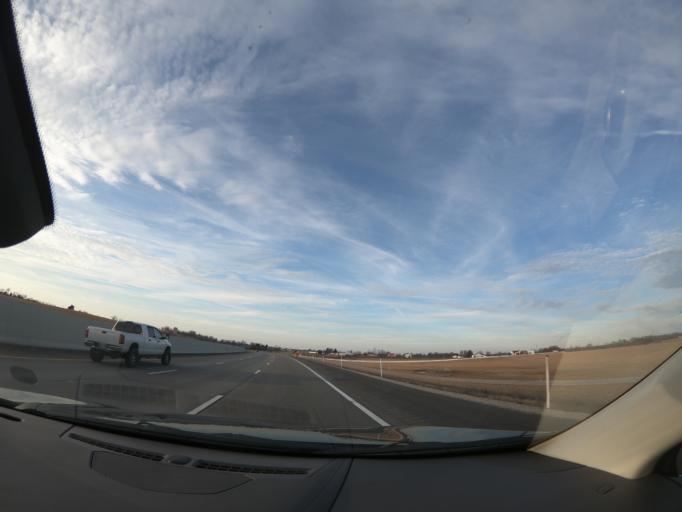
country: US
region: Kentucky
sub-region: Larue County
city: Hodgenville
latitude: 37.4934
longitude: -85.8811
